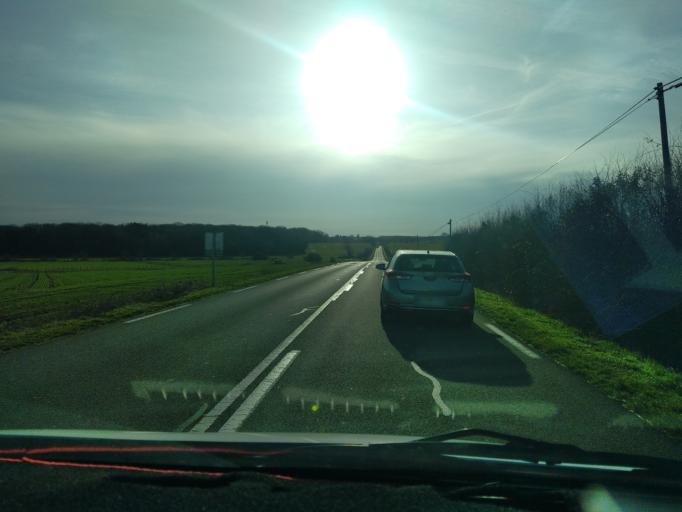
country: FR
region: Franche-Comte
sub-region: Departement de la Haute-Saone
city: Gray
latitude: 47.3715
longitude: 5.6663
